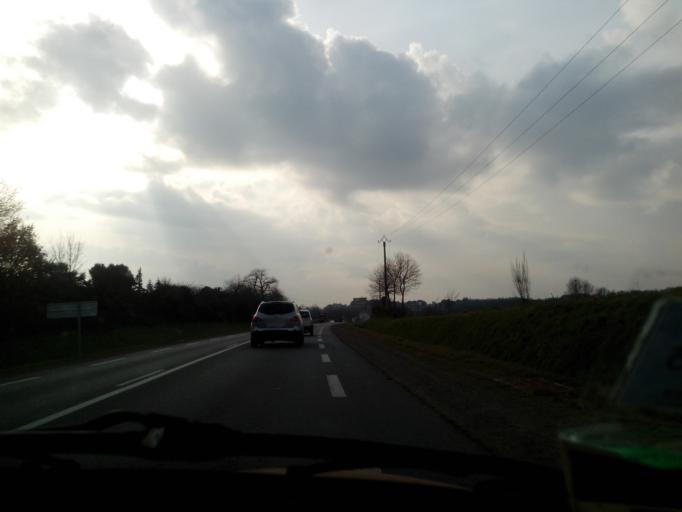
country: FR
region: Brittany
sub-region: Departement du Morbihan
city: Loyat
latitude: 48.0160
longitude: -2.3308
